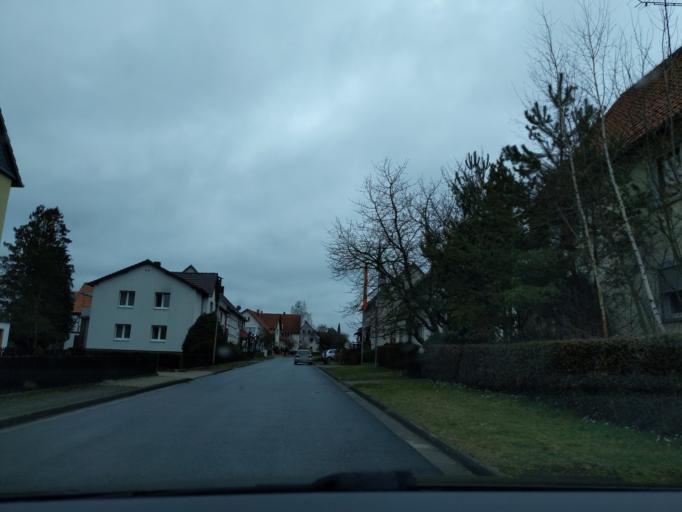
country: DE
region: Hesse
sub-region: Regierungsbezirk Kassel
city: Volkmarsen
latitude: 51.3471
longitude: 9.0868
